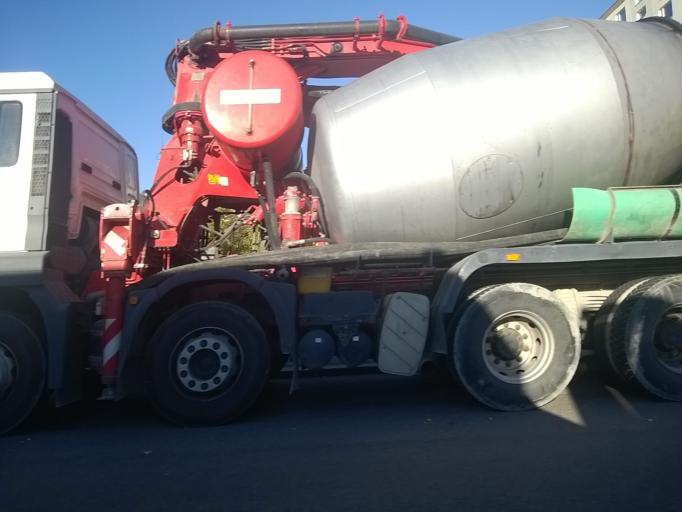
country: FI
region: Pirkanmaa
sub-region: Tampere
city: Tampere
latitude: 61.4520
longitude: 23.8375
